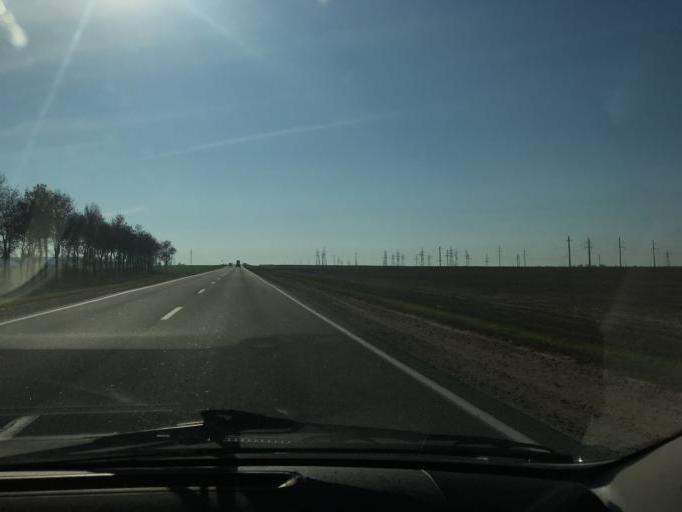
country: BY
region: Minsk
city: Salihorsk
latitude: 52.8674
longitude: 27.4671
